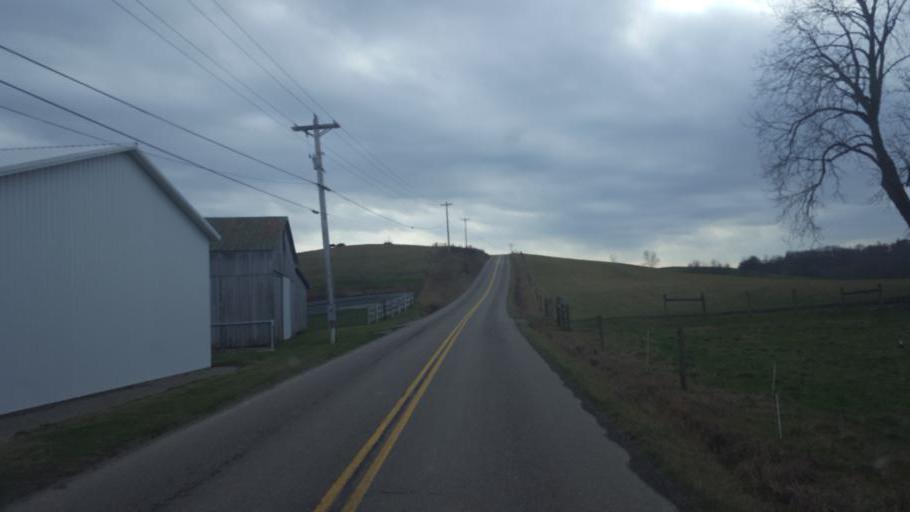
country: US
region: Ohio
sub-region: Gallia County
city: Gallipolis
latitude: 38.7598
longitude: -82.3702
